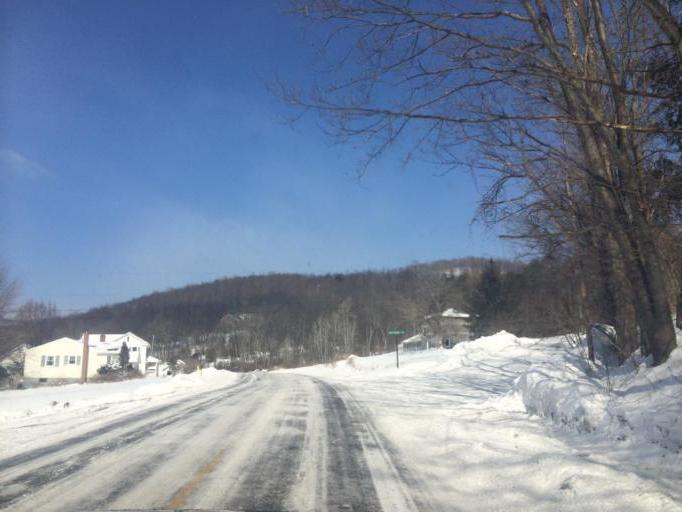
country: US
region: Pennsylvania
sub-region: Centre County
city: Stormstown
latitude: 40.8472
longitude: -78.0036
